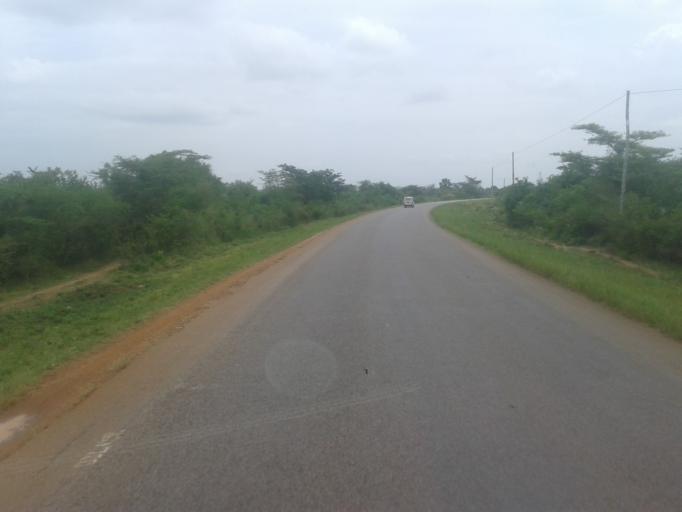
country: UG
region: Western Region
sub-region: Kiryandongo District
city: Masindi Port
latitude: 1.5216
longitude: 32.0468
